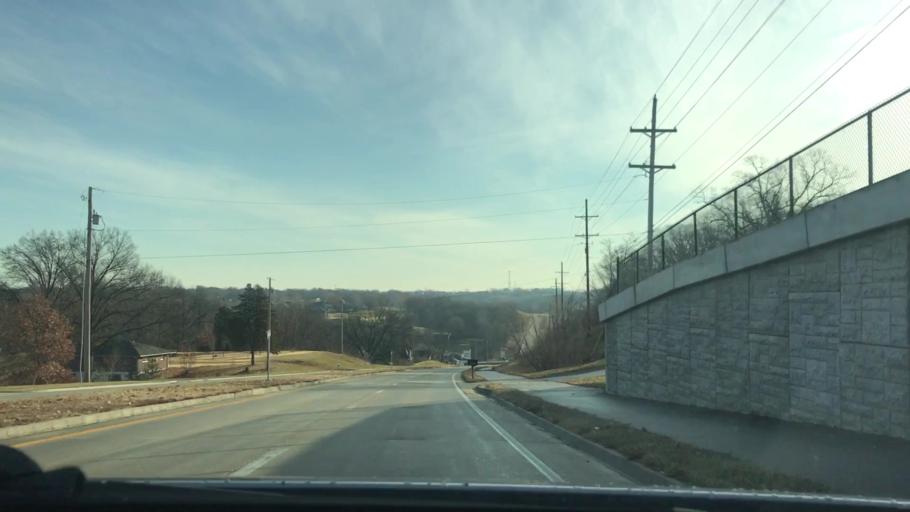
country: US
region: Missouri
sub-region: Platte County
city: Weatherby Lake
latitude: 39.2117
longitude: -94.7198
